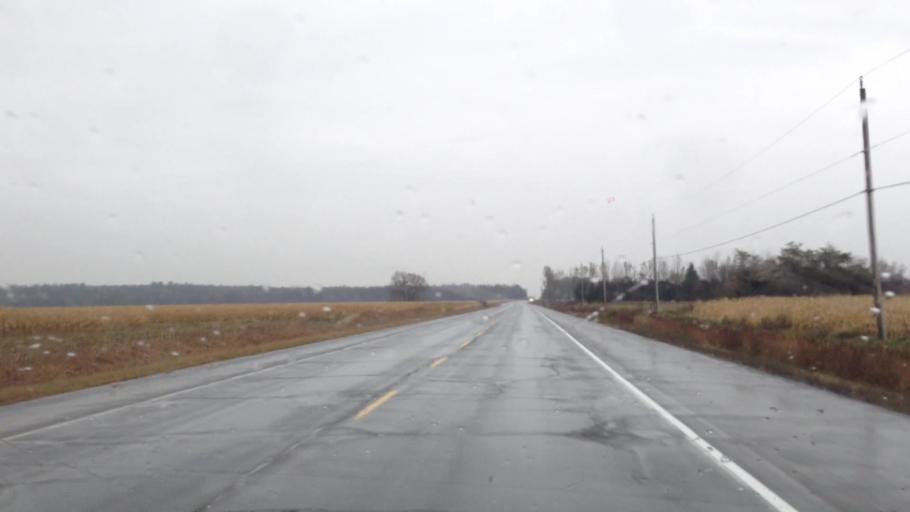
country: CA
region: Ontario
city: Clarence-Rockland
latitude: 45.4446
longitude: -75.4206
